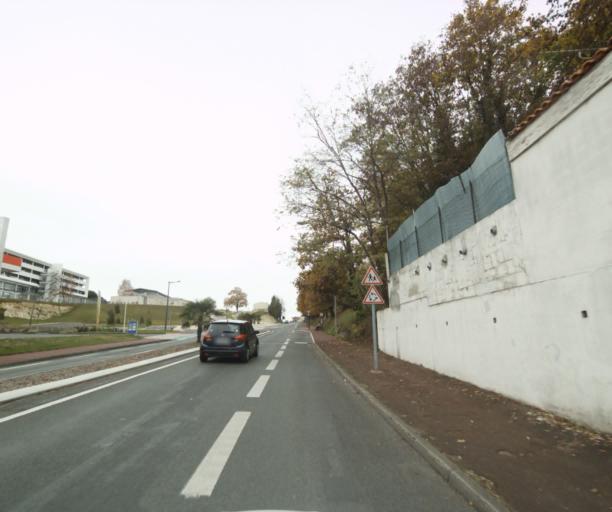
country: FR
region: Poitou-Charentes
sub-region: Departement de la Charente-Maritime
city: Saintes
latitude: 45.7396
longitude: -0.6425
